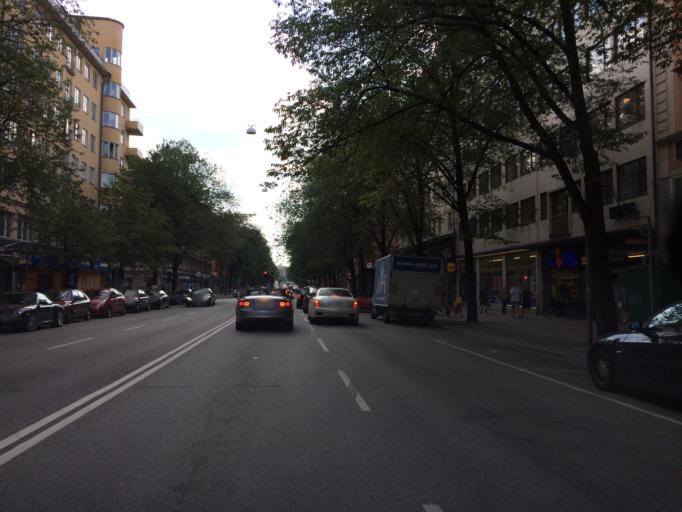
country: SE
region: Stockholm
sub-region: Stockholms Kommun
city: Stockholm
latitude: 59.3412
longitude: 18.0581
